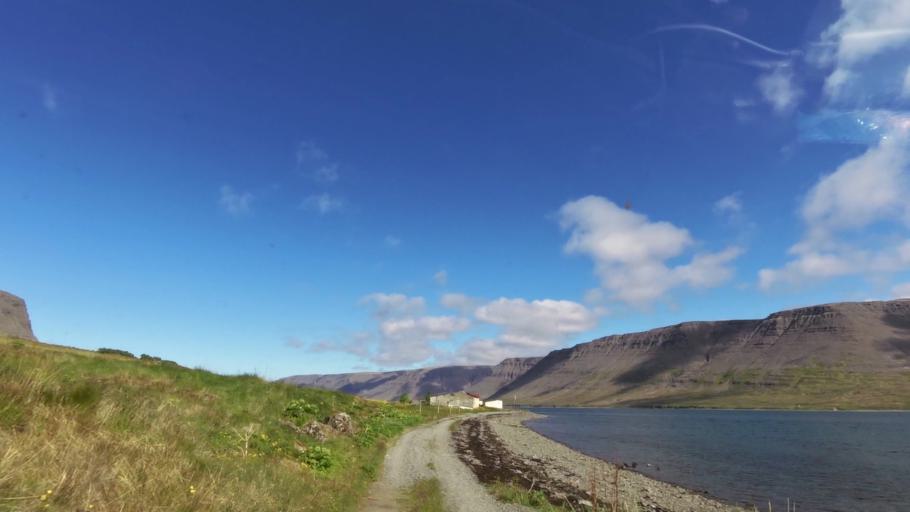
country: IS
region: West
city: Olafsvik
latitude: 65.6199
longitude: -23.8672
